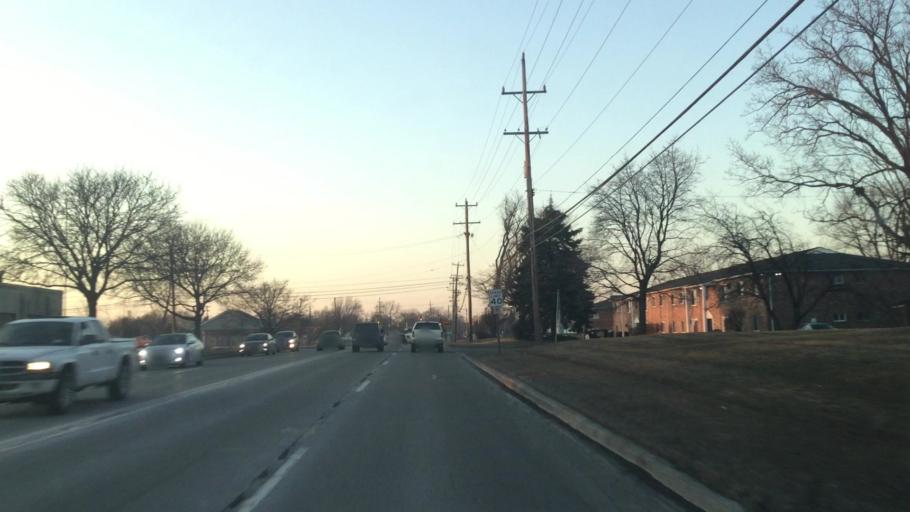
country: US
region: Michigan
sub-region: Wayne County
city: Livonia
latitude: 42.3440
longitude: -83.3498
